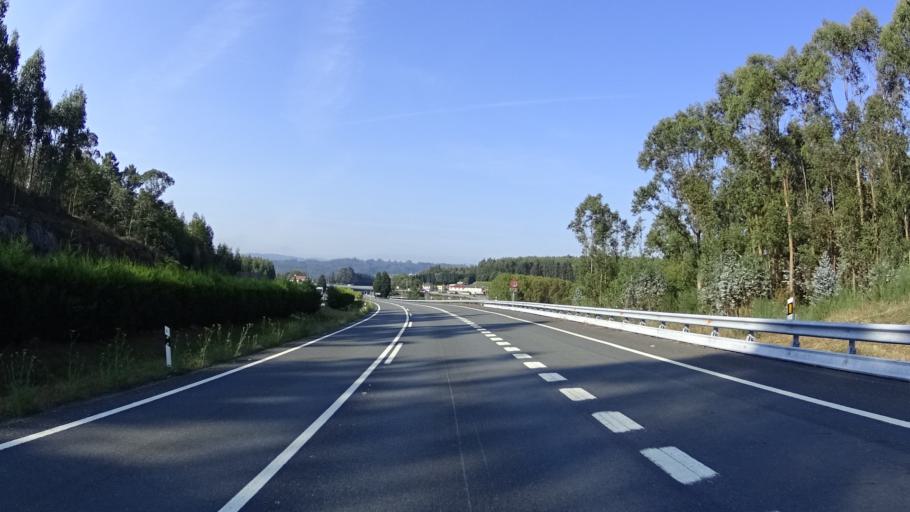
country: ES
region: Galicia
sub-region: Provincia da Coruna
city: Coiros
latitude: 43.2450
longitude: -8.1549
